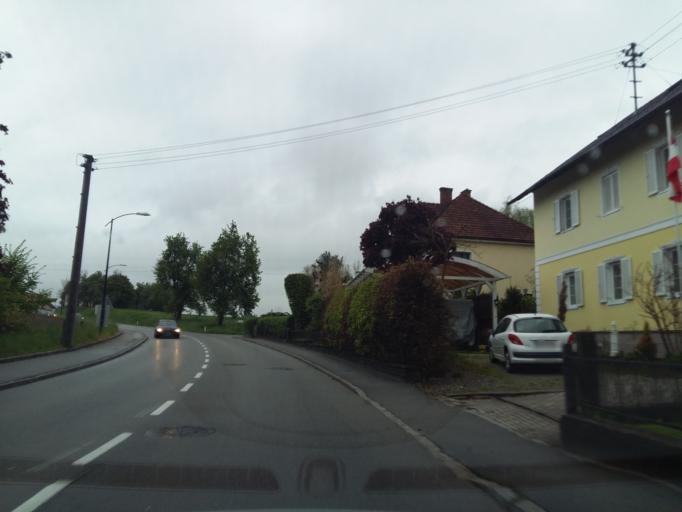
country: AT
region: Upper Austria
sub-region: Politischer Bezirk Scharding
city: Sankt Marienkirchen bei Schaerding
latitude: 48.4094
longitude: 13.4309
